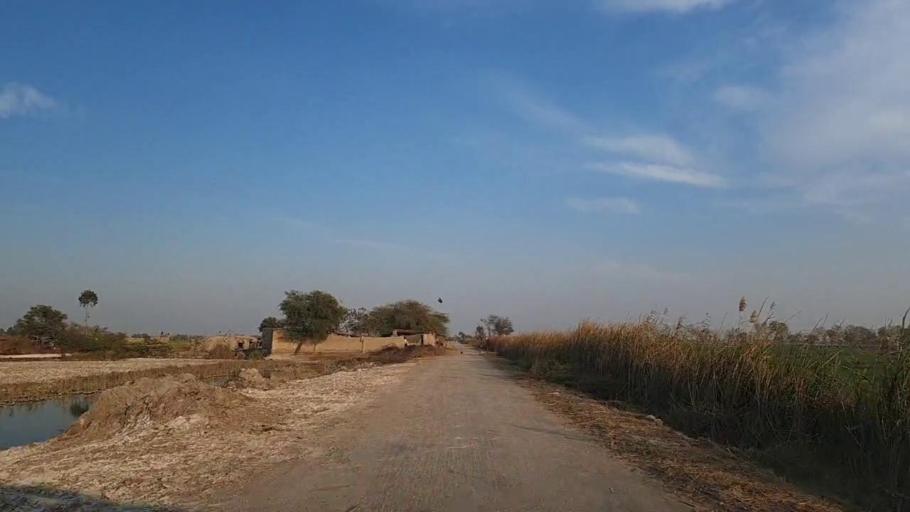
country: PK
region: Sindh
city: Bandhi
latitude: 26.5744
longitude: 68.3417
